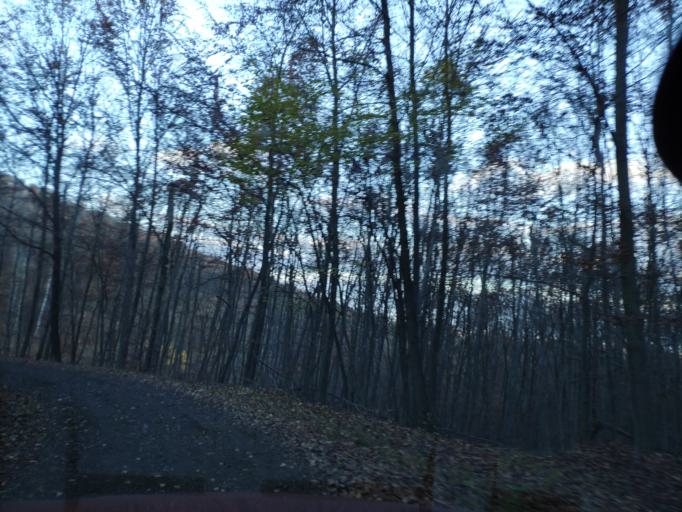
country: SK
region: Kosicky
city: Secovce
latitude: 48.6011
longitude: 21.5146
